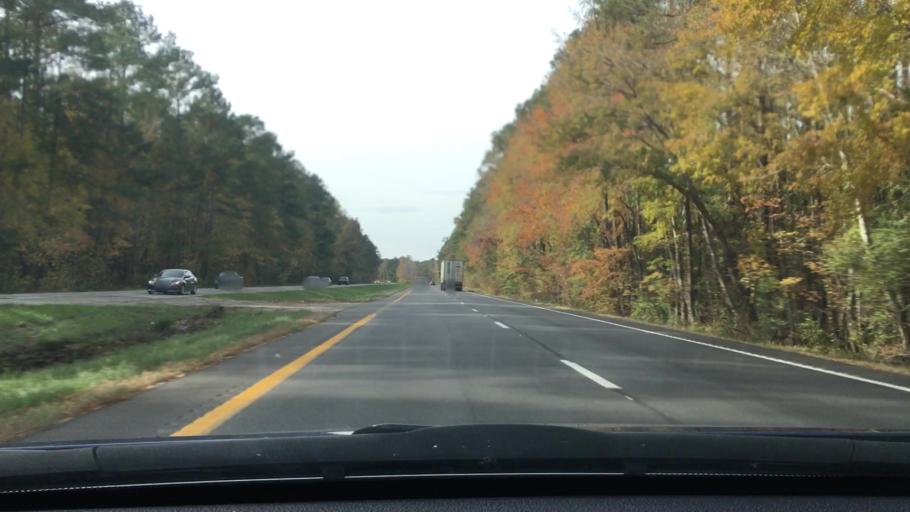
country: US
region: South Carolina
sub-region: Sumter County
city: Stateburg
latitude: 33.9510
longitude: -80.5567
